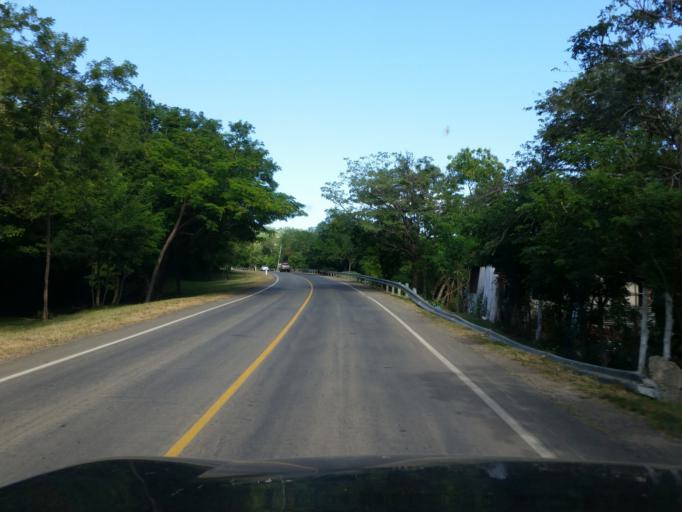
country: NI
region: Rivas
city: San Juan del Sur
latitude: 11.2644
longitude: -85.8503
